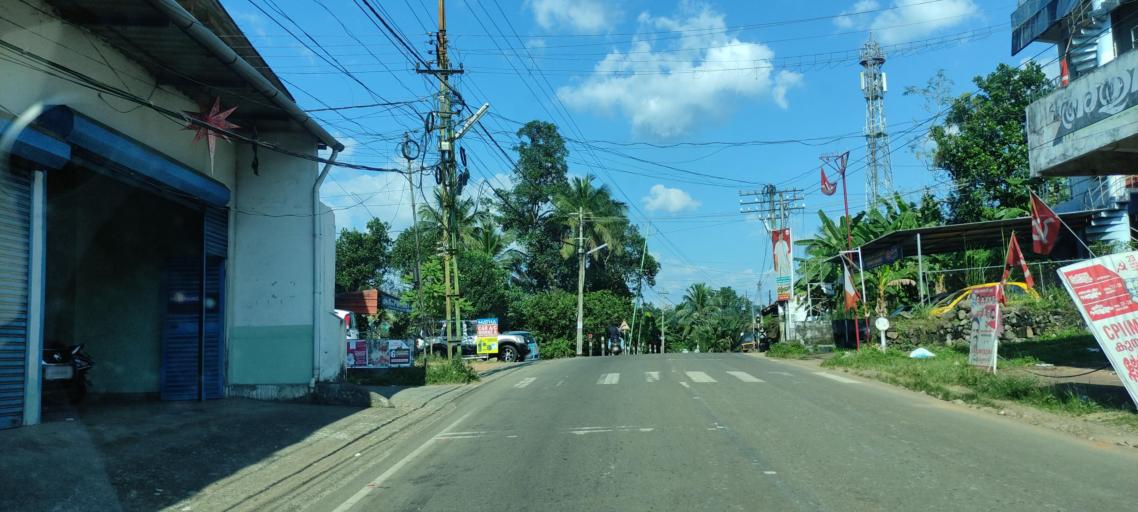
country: IN
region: Kerala
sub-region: Pattanamtitta
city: Pathanamthitta
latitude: 9.2675
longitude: 76.7947
